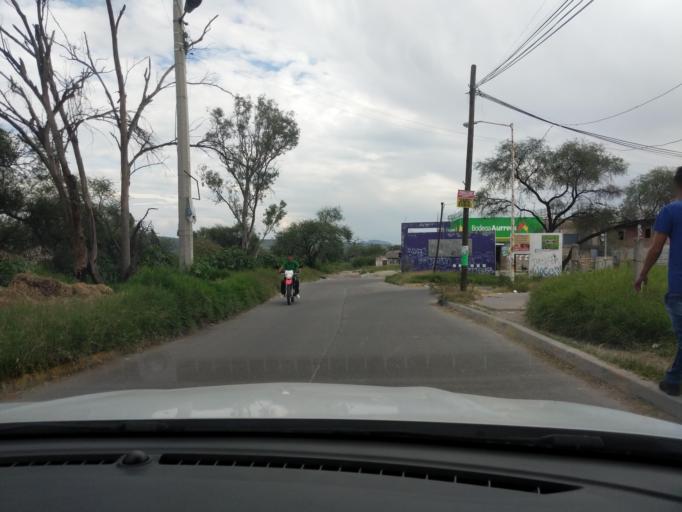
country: MX
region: Jalisco
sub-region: El Salto
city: Galaxia Bonito Jalisco
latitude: 20.5104
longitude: -103.1900
